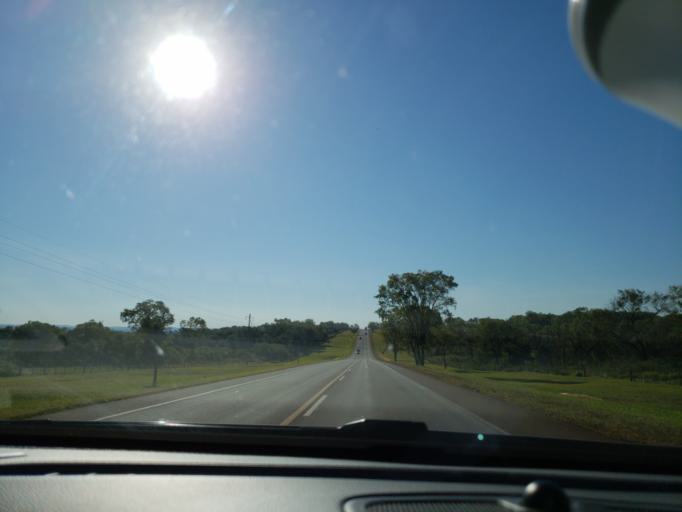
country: AR
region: Misiones
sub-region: Departamento de Apostoles
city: San Jose
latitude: -27.7219
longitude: -55.7916
